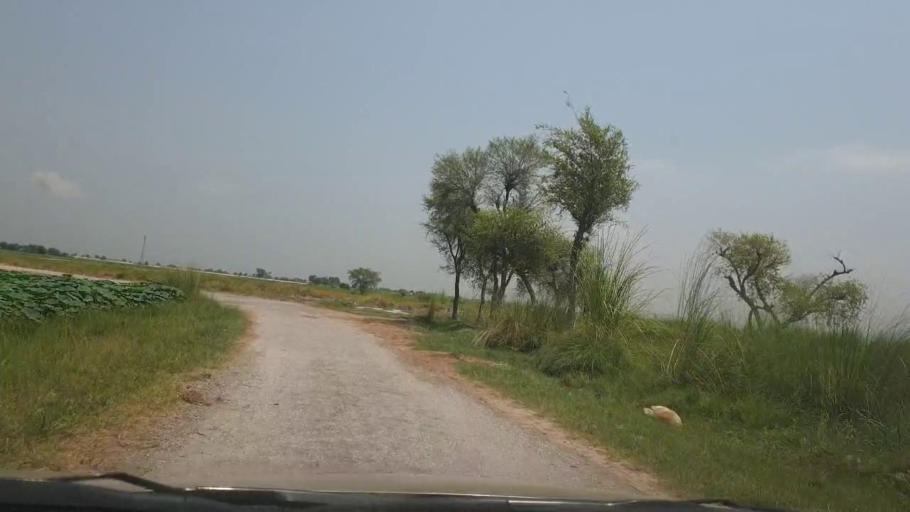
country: PK
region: Sindh
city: Ratodero
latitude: 27.7329
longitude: 68.3129
